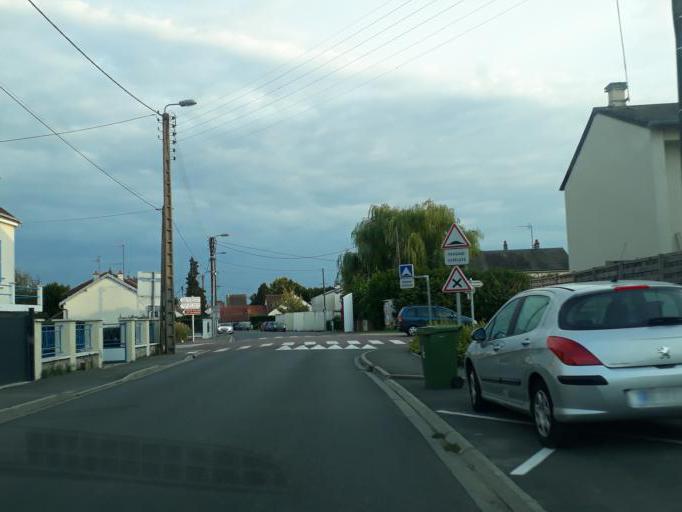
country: FR
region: Centre
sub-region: Departement du Loiret
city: Saran
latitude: 47.9296
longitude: 1.8862
